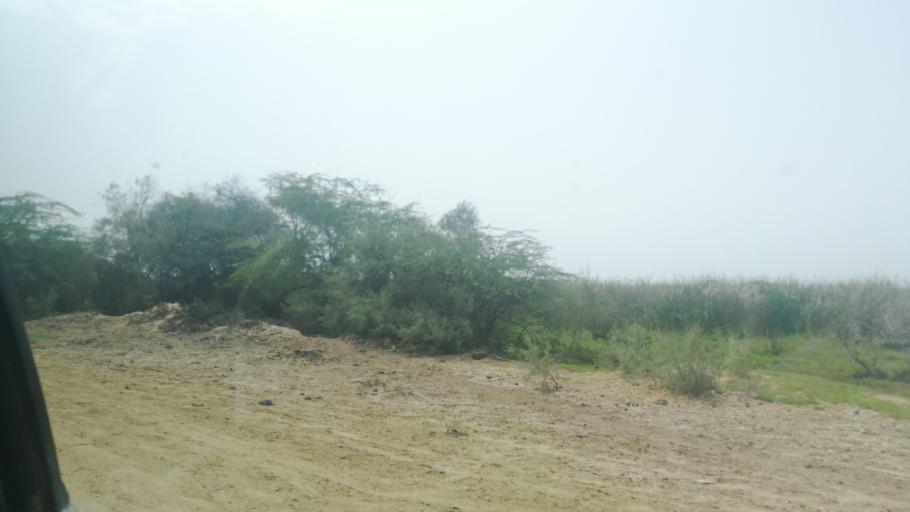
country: SN
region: Saint-Louis
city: Saint-Louis
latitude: 16.0595
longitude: -16.3258
